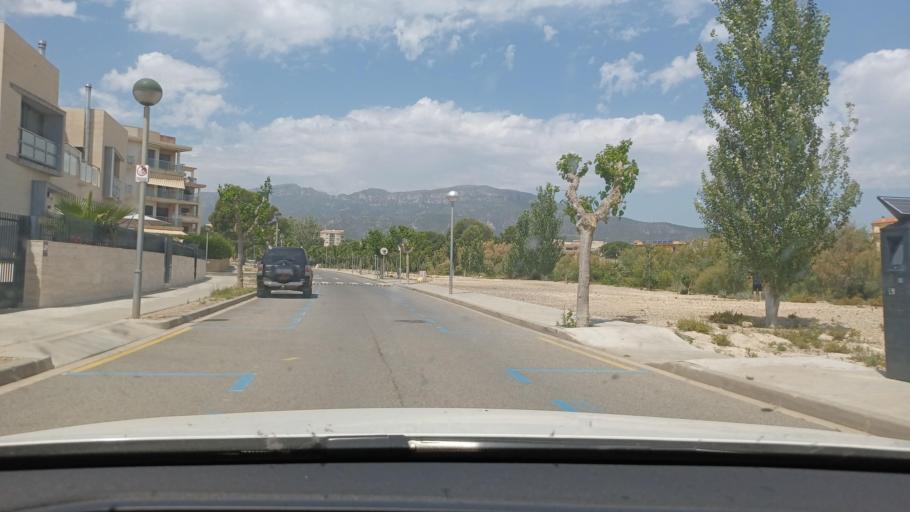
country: ES
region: Catalonia
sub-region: Provincia de Tarragona
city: Colldejou
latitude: 40.9922
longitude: 0.9290
